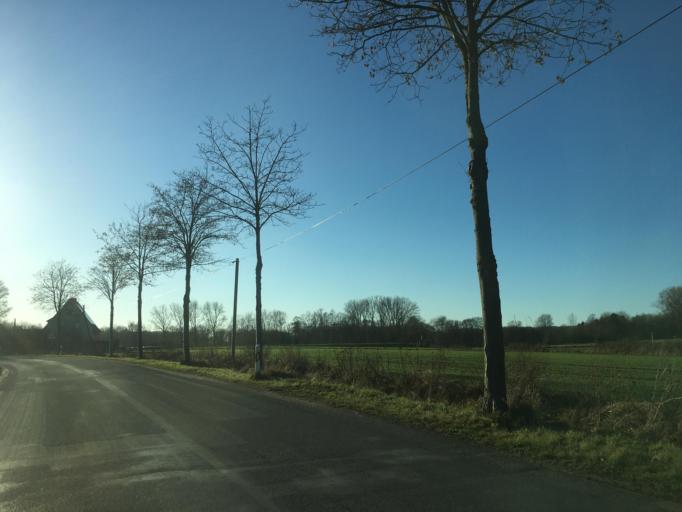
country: DE
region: North Rhine-Westphalia
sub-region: Regierungsbezirk Munster
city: Dulmen
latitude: 51.8560
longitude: 7.2923
